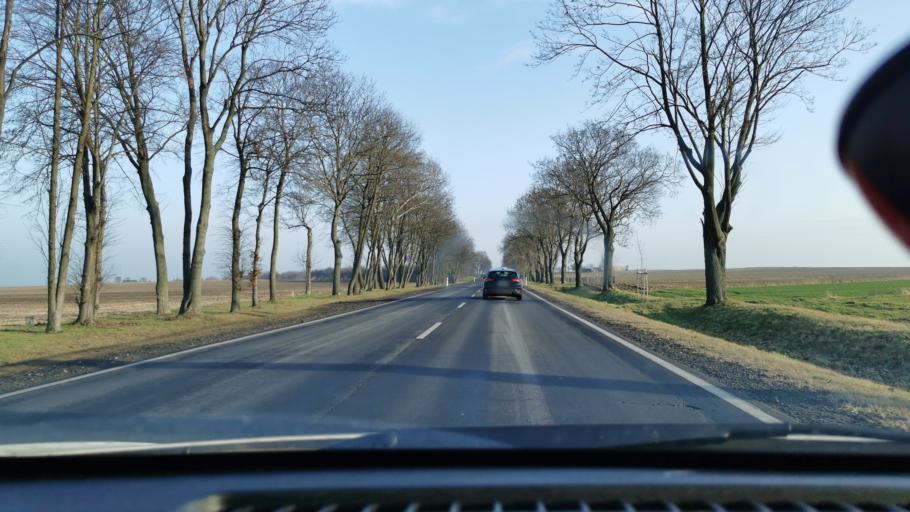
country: PL
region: Lodz Voivodeship
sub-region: Powiat sieradzki
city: Wroblew
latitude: 51.6195
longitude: 18.5891
